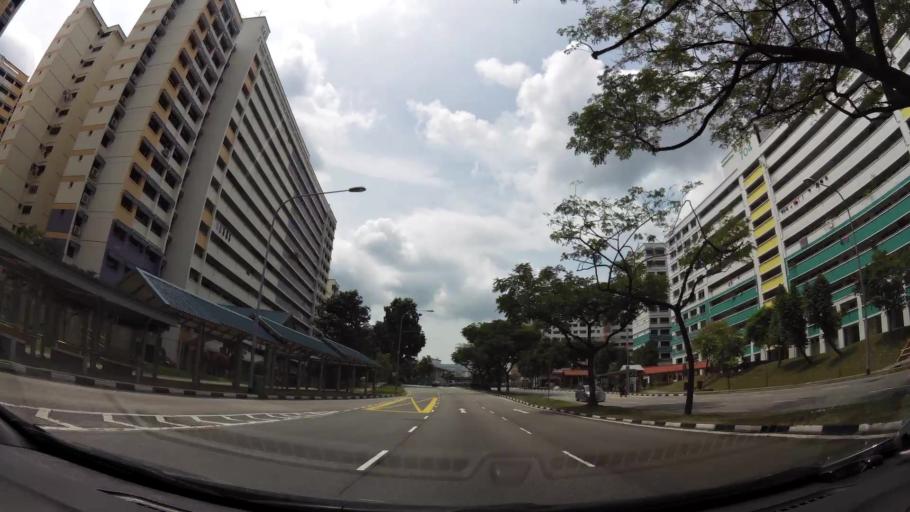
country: MY
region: Johor
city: Johor Bahru
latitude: 1.3409
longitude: 103.6959
